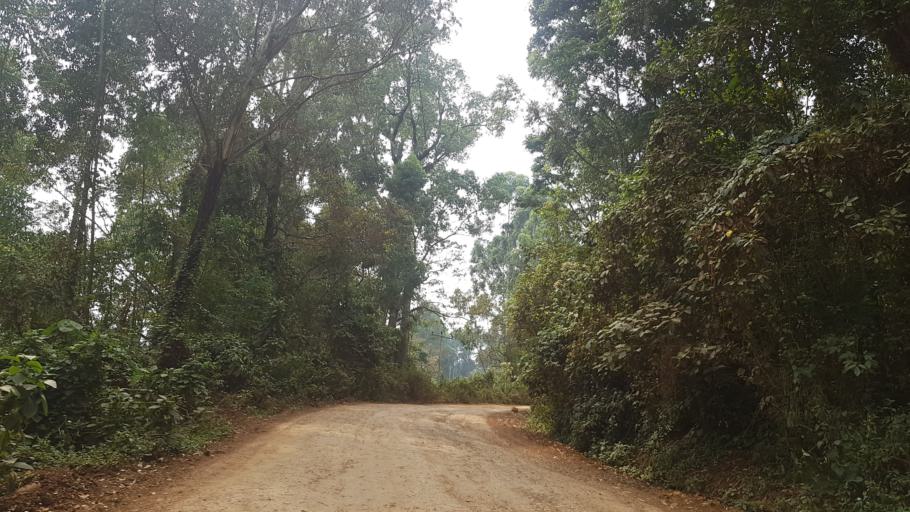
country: ET
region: Oromiya
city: Gore
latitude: 7.8212
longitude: 35.4589
